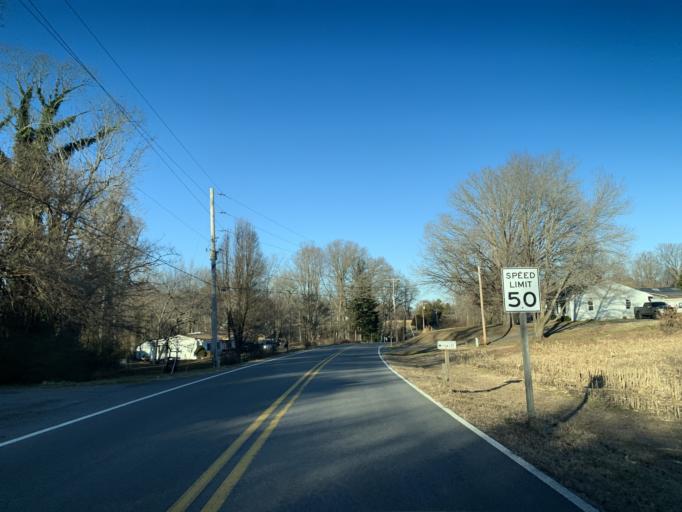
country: US
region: Maryland
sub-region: Saint Mary's County
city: Mechanicsville
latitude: 38.4195
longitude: -76.6942
